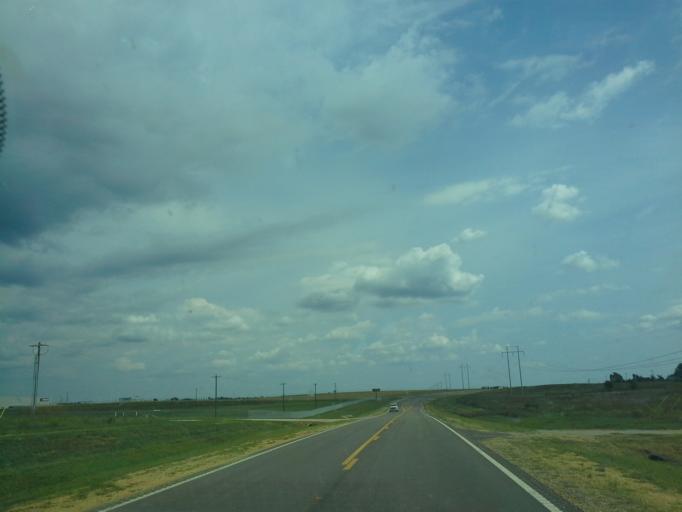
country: US
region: Mississippi
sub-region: Clay County
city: West Point
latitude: 33.6378
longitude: -88.6114
